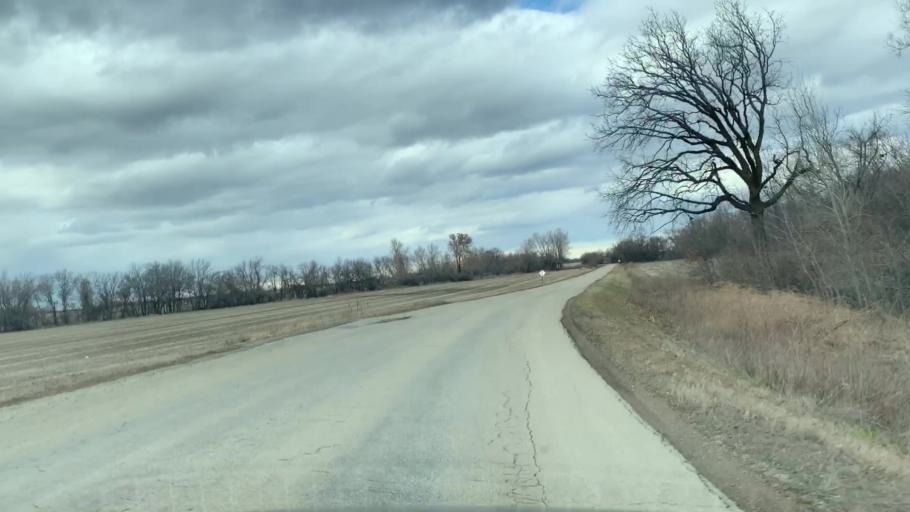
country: US
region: Kansas
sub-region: Allen County
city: Humboldt
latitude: 37.8054
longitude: -95.4717
